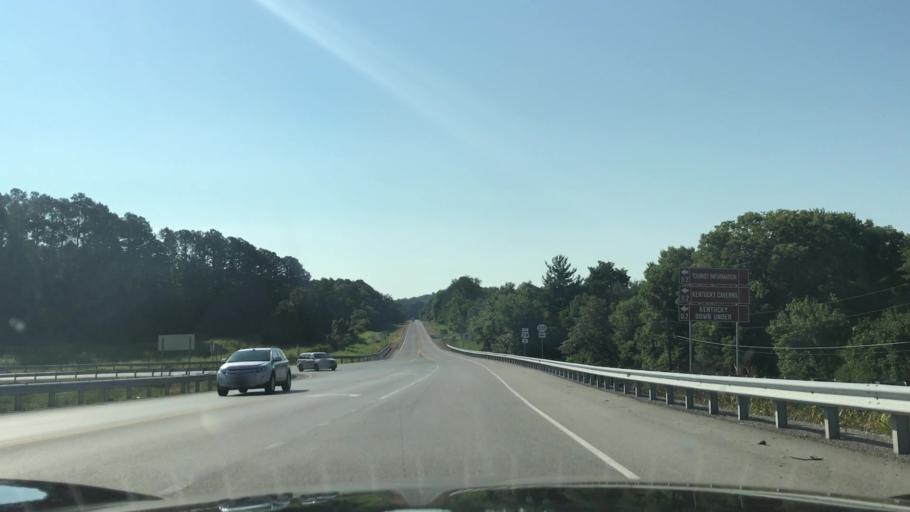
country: US
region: Kentucky
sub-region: Hart County
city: Horse Cave
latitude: 37.2003
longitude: -85.9358
